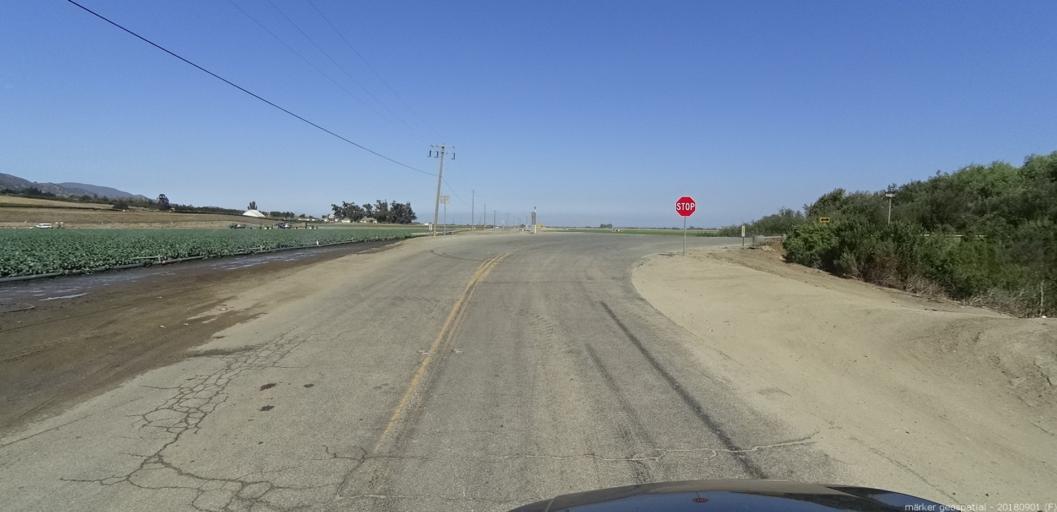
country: US
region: California
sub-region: Monterey County
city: Chualar
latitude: 36.5558
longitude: -121.5500
